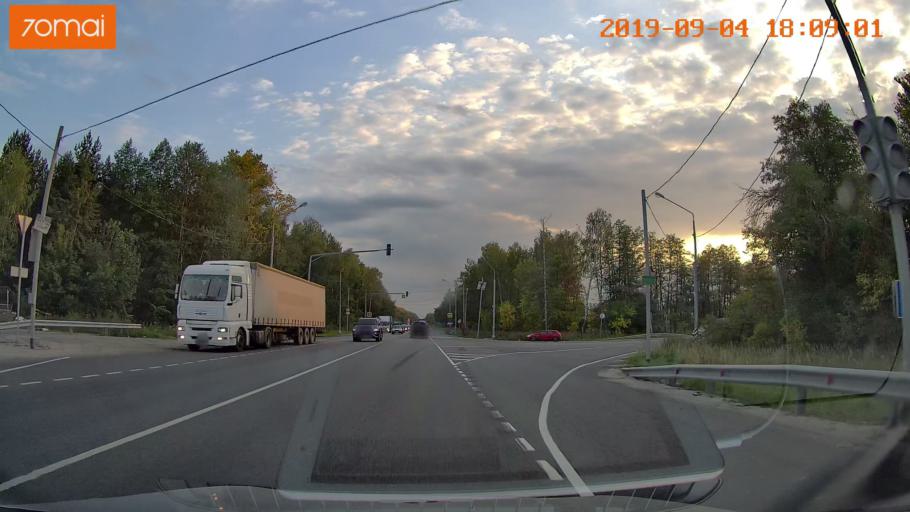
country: RU
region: Moskovskaya
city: Khorlovo
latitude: 55.3995
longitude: 38.7786
